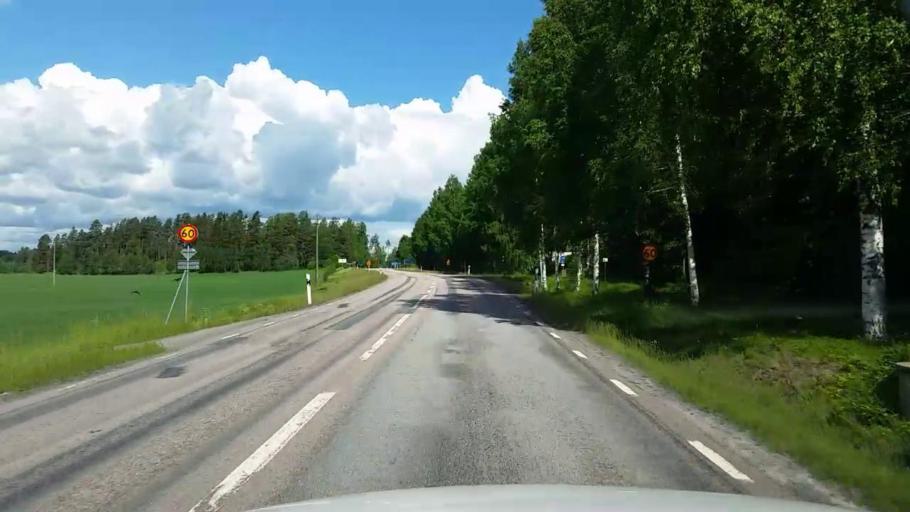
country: SE
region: Vaestmanland
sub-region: Kopings Kommun
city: Kolsva
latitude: 59.6786
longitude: 15.7648
